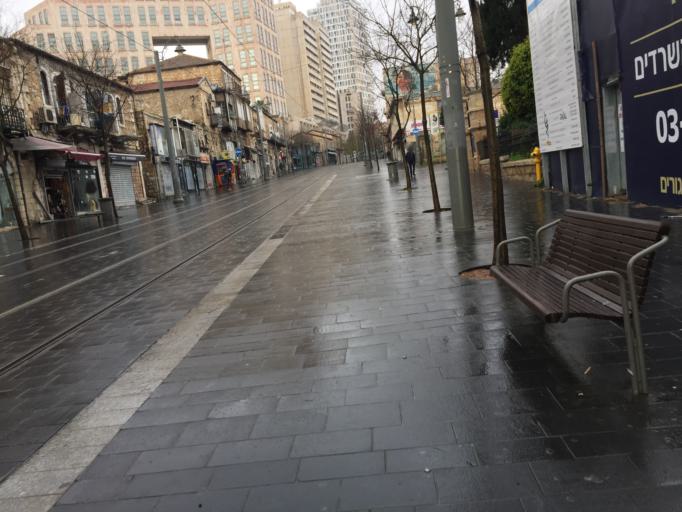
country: IL
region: Jerusalem
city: West Jerusalem
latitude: 31.7836
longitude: 35.2172
